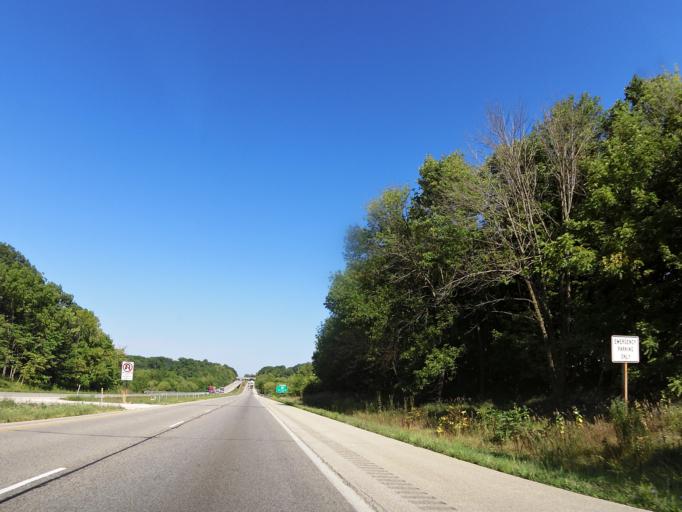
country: US
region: Illinois
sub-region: Vermilion County
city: Tilton
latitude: 40.1121
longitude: -87.6879
